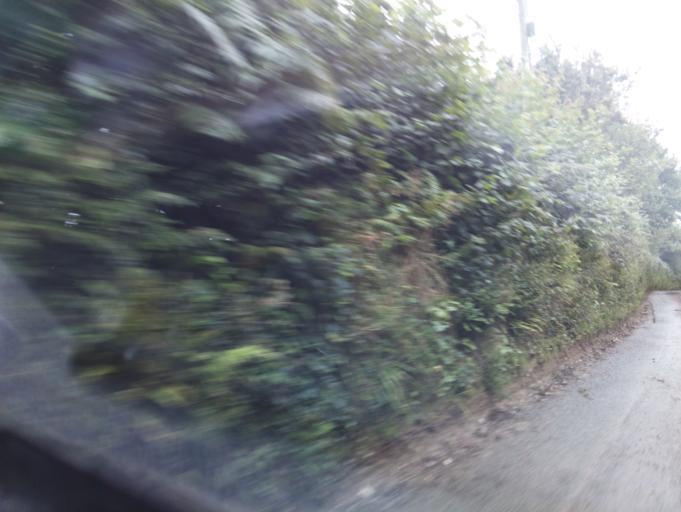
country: GB
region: England
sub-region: Devon
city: Totnes
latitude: 50.3417
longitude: -3.6845
